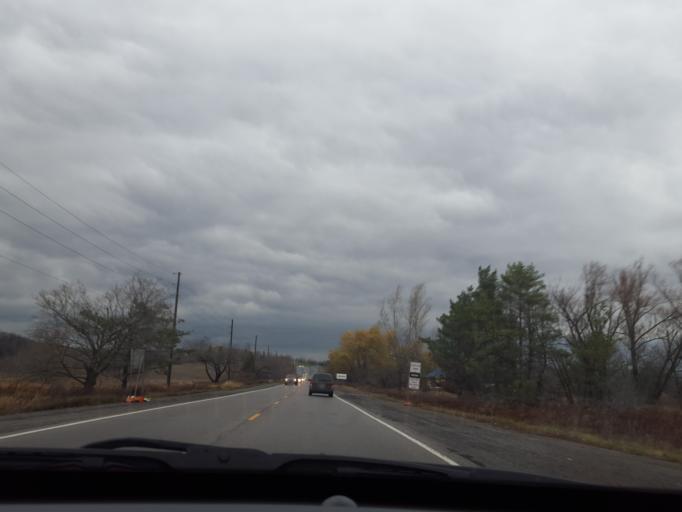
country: CA
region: Ontario
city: Pickering
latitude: 43.8948
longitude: -79.0941
